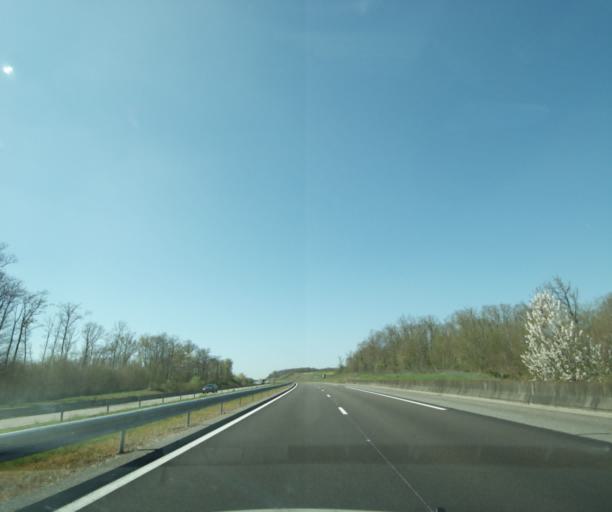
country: FR
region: Centre
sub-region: Departement du Loiret
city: Bonny-sur-Loire
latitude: 47.6071
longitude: 2.8305
